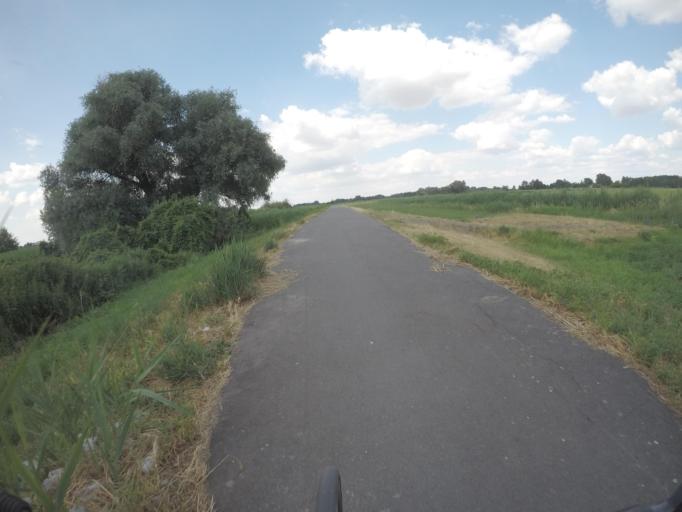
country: DE
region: Brandenburg
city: Roskow
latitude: 52.4537
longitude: 12.7650
